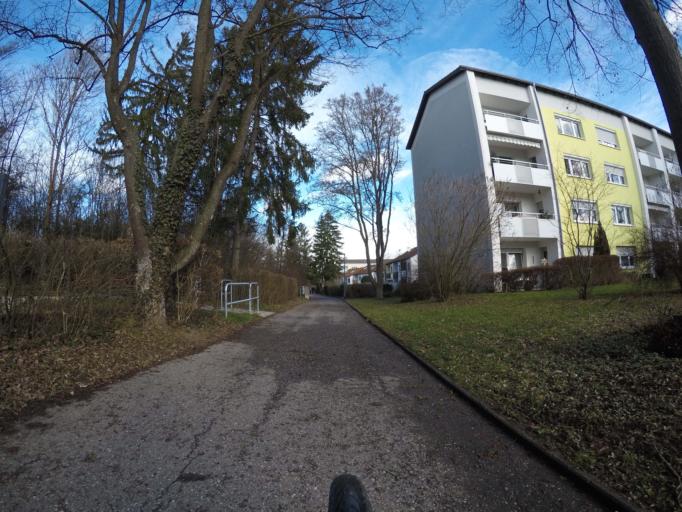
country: DE
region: Baden-Wuerttemberg
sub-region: Tuebingen Region
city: Sickenhausen
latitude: 48.5190
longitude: 9.2014
